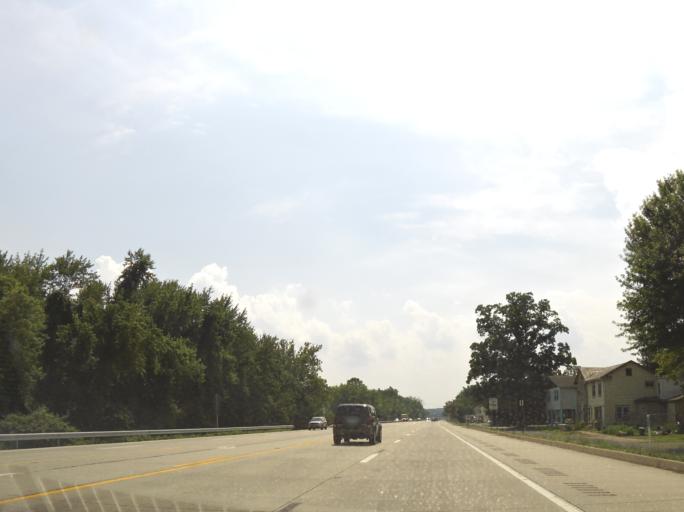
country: US
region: Pennsylvania
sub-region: Dauphin County
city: Matamoras
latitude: 40.4538
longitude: -76.9682
